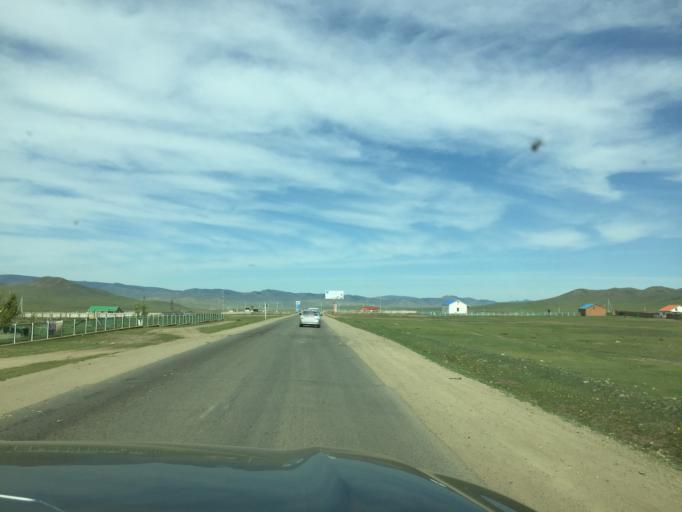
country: MN
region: Central Aimak
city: Ihsueuej
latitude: 48.2270
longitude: 106.2888
